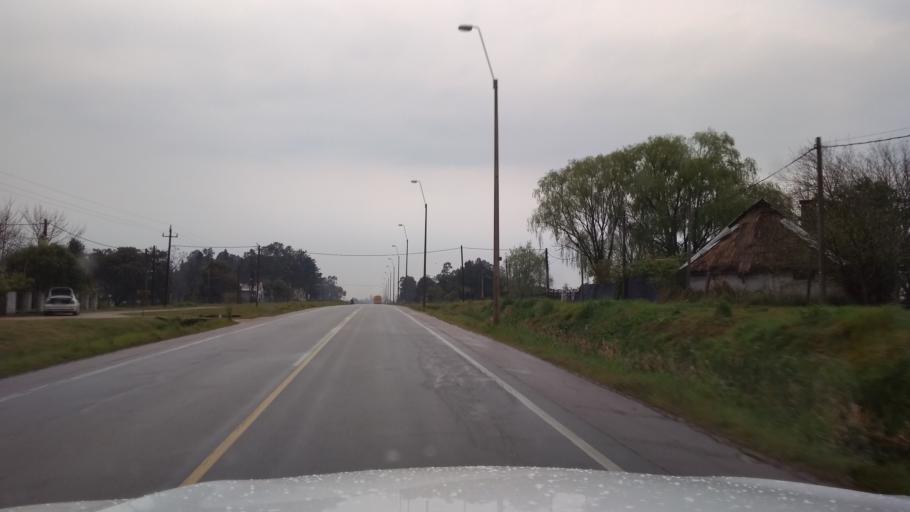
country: UY
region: Canelones
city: Toledo
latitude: -34.7628
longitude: -56.1177
